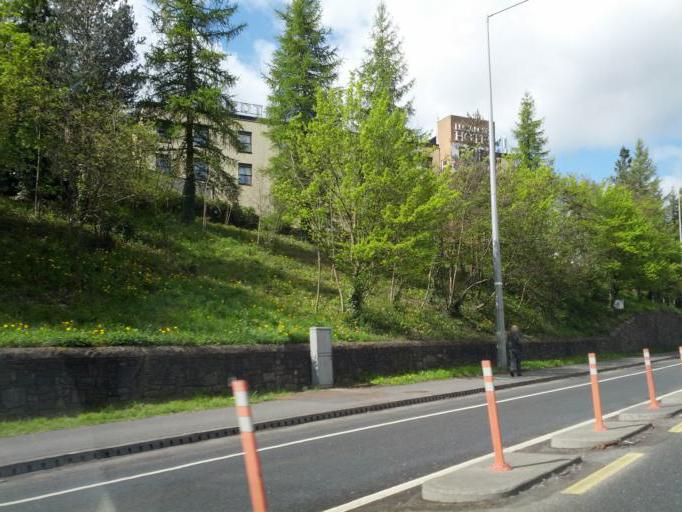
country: IE
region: Leinster
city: Lucan
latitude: 53.3557
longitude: -6.4625
